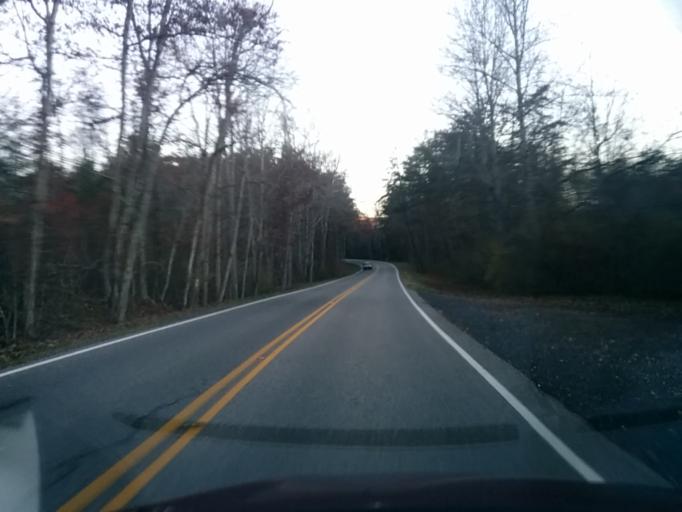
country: US
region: Virginia
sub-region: Rockbridge County
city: East Lexington
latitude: 37.9497
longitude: -79.4650
